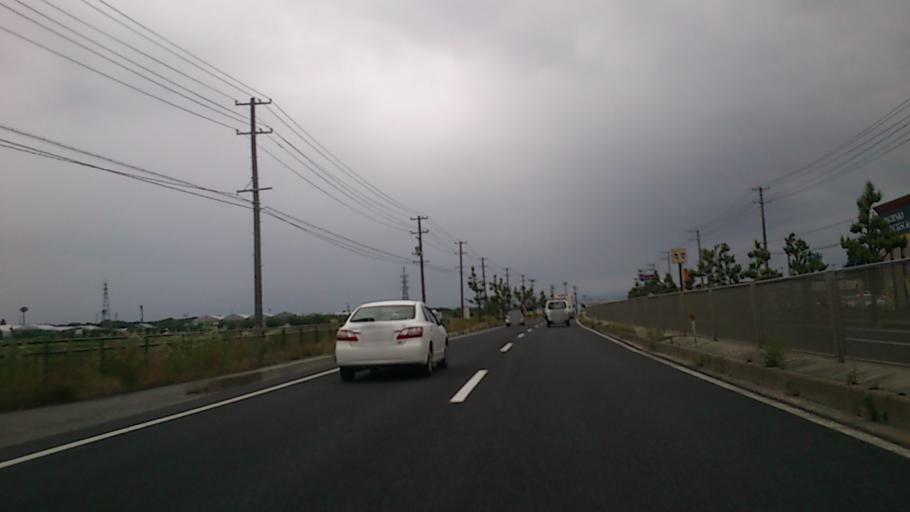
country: JP
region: Yamagata
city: Tendo
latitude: 38.3491
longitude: 140.3839
